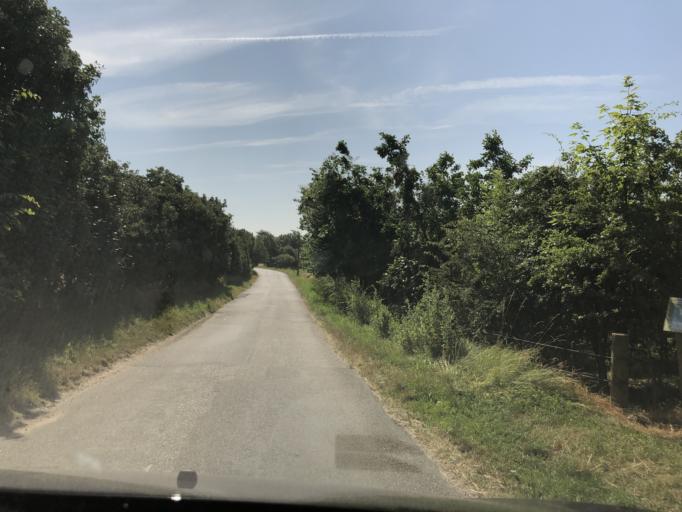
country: DK
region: South Denmark
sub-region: Faaborg-Midtfyn Kommune
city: Faaborg
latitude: 54.9425
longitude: 10.2488
